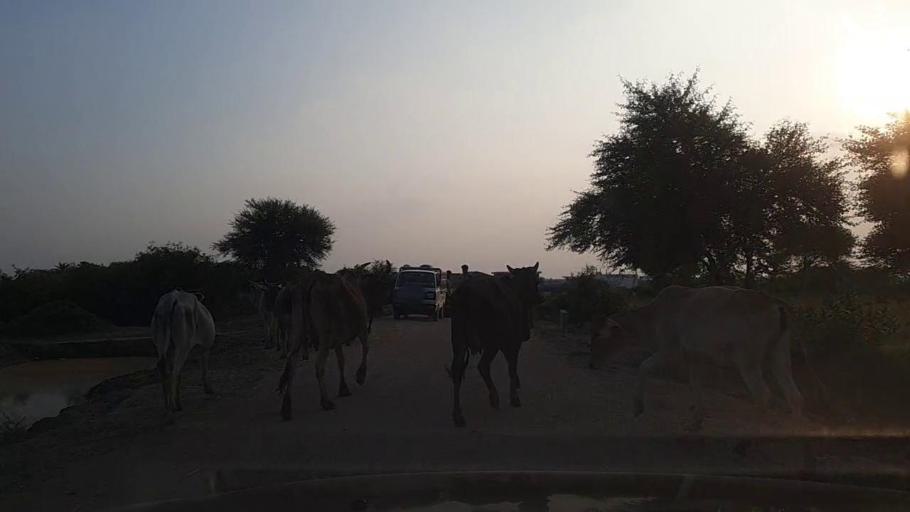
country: PK
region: Sindh
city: Jati
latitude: 24.5330
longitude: 68.3575
